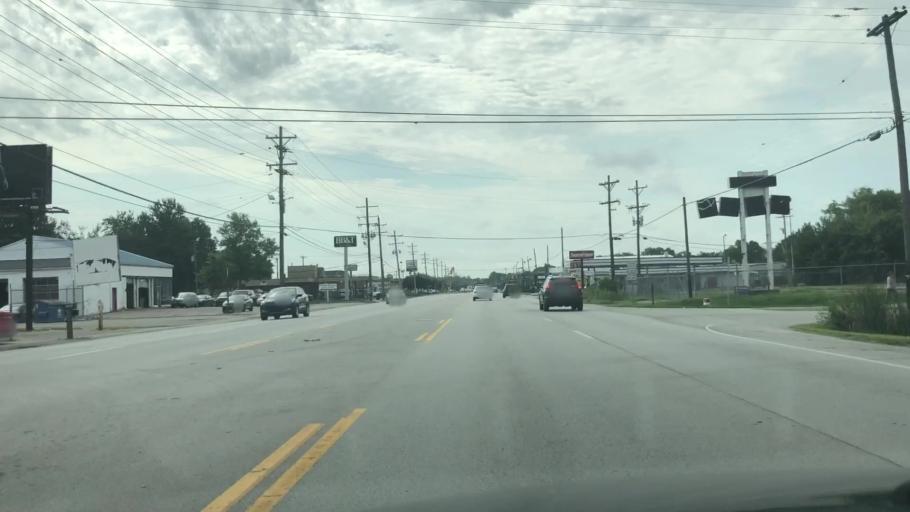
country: US
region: Kentucky
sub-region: Jefferson County
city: Audubon Park
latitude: 38.1721
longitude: -85.7101
